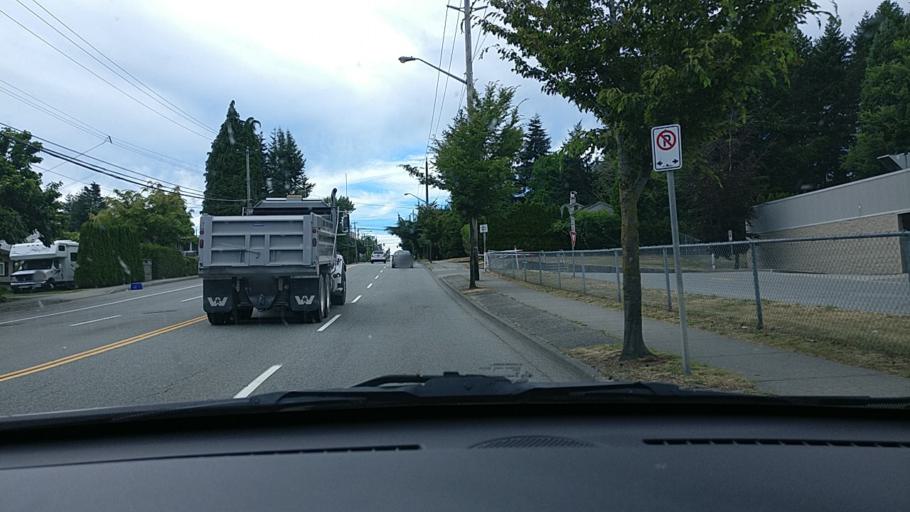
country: CA
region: British Columbia
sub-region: Greater Vancouver Regional District
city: White Rock
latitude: 49.0312
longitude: -122.7857
